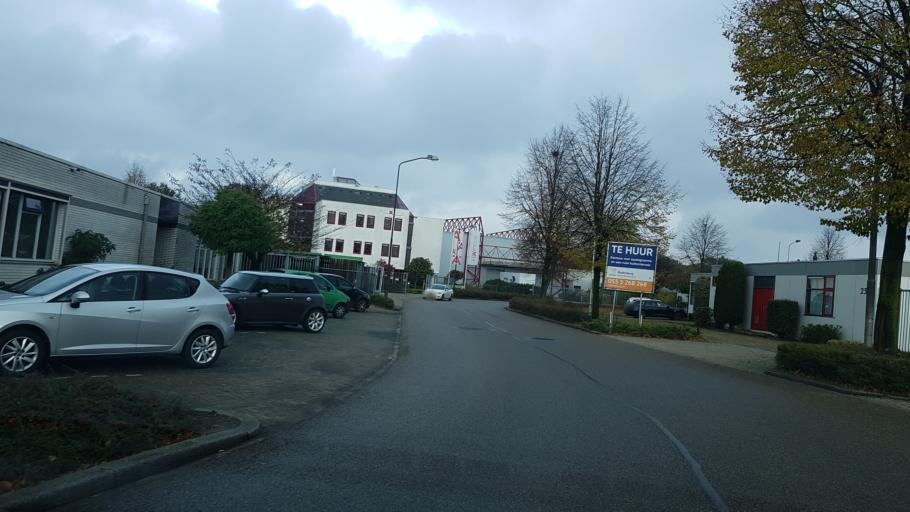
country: NL
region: Gelderland
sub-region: Gemeente Apeldoorn
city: Beekbergen
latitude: 52.1812
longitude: 5.9777
